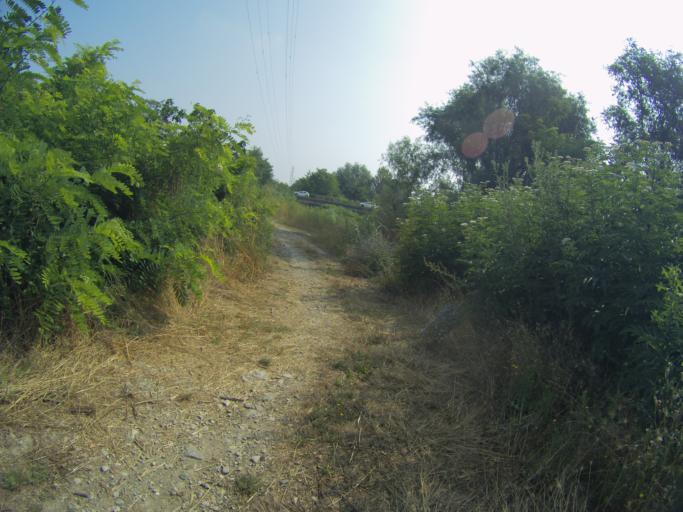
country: IT
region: Emilia-Romagna
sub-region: Provincia di Reggio Emilia
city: Pratissolo
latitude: 44.5950
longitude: 10.6756
